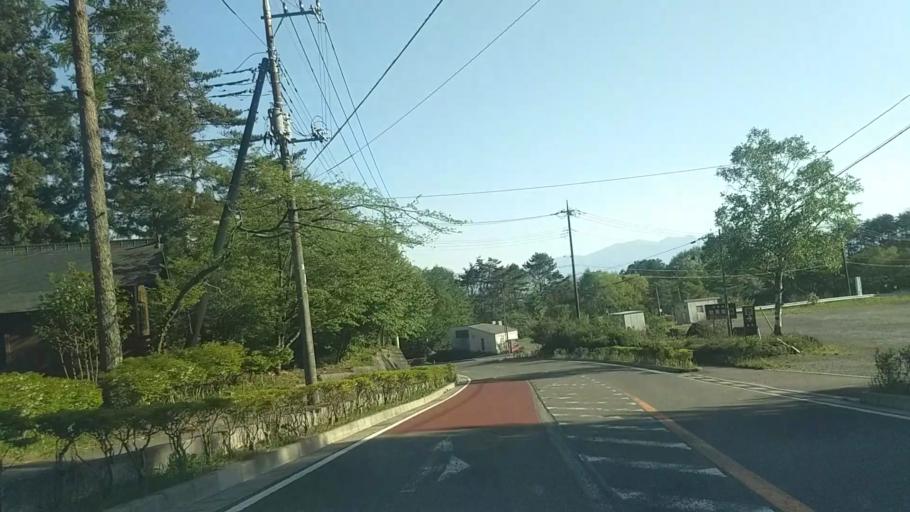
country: JP
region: Yamanashi
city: Nirasaki
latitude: 35.9199
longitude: 138.4352
